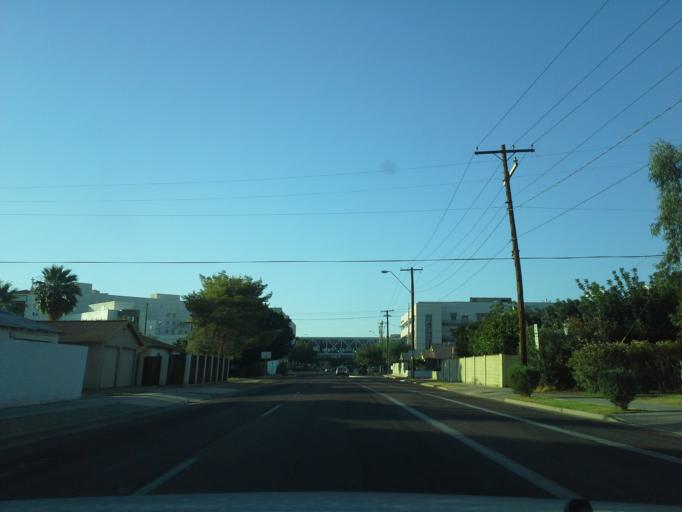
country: US
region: Arizona
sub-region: Maricopa County
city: Phoenix
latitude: 33.4787
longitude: -112.0782
